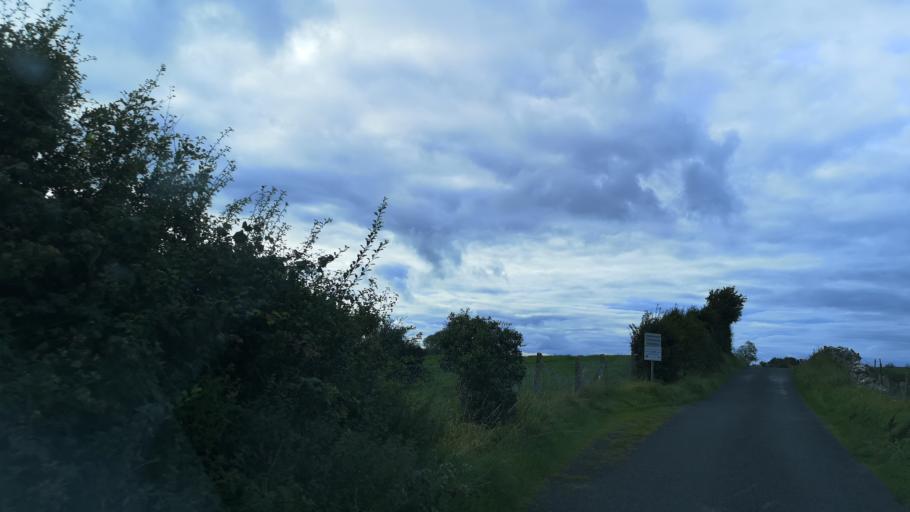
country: IE
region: Connaught
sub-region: County Galway
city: Ballinasloe
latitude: 53.3763
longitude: -8.1709
